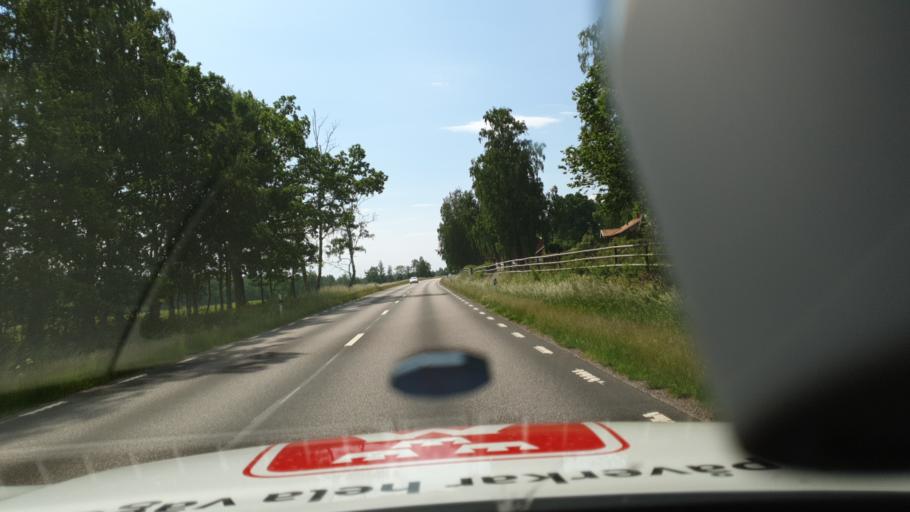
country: SE
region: Vaestra Goetaland
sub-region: Hjo Kommun
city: Hjo
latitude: 58.1528
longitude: 14.2139
